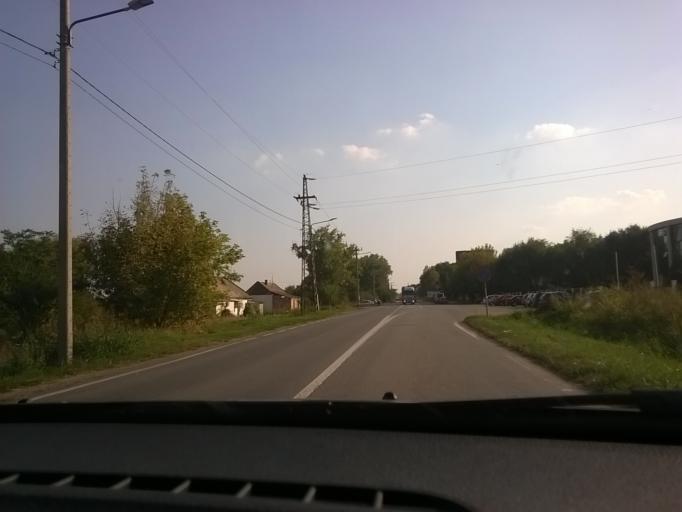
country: RS
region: Autonomna Pokrajina Vojvodina
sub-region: Juznobanatski Okrug
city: Vrsac
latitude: 45.1375
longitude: 21.2873
